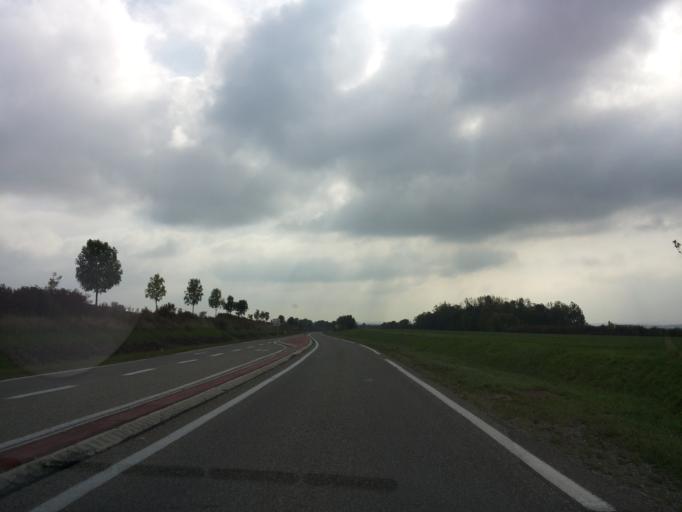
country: FR
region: Lorraine
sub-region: Departement de la Moselle
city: Solgne
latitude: 48.9214
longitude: 6.3334
